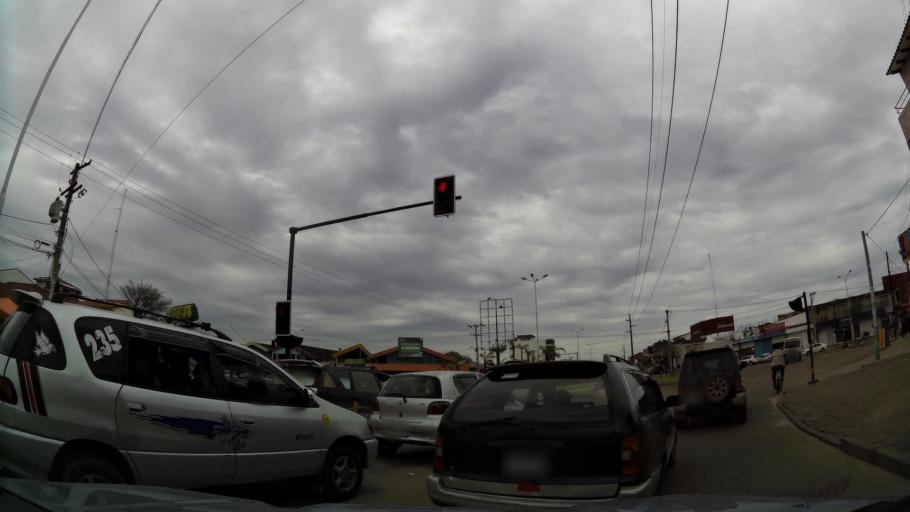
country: BO
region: Santa Cruz
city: Santa Cruz de la Sierra
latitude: -17.7771
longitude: -63.2036
